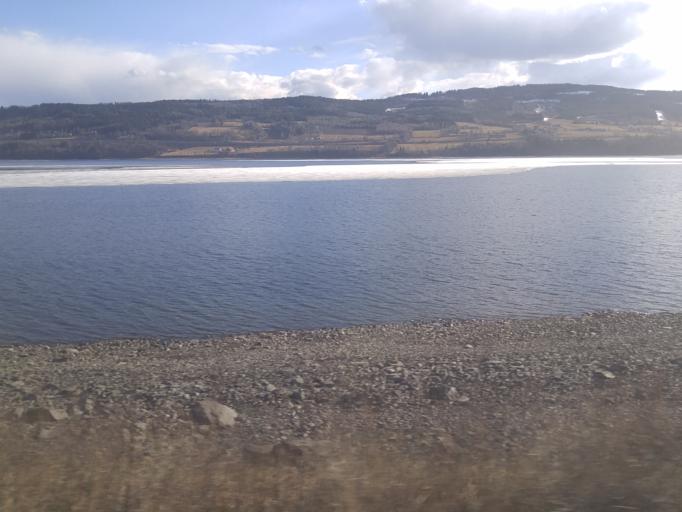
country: NO
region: Hedmark
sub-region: Ringsaker
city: Moelv
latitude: 61.0024
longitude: 10.5755
